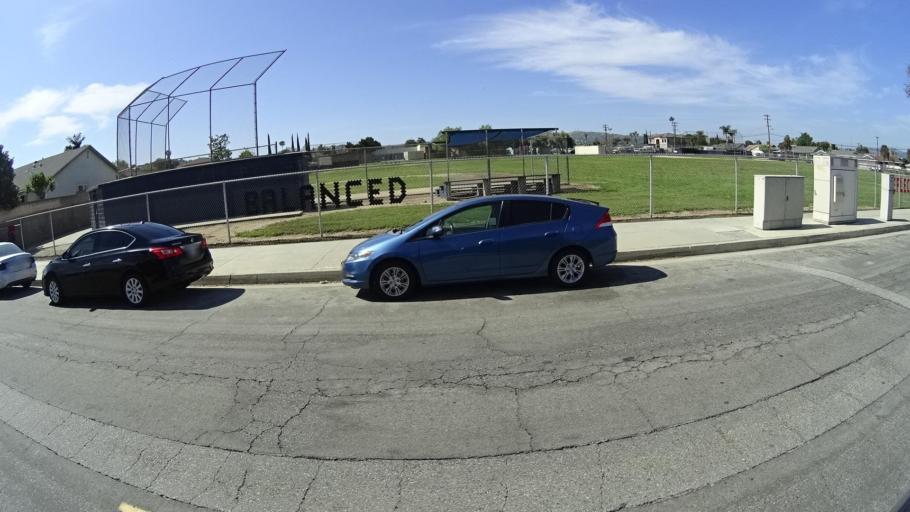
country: US
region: California
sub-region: Los Angeles County
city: Walnut
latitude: 33.9931
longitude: -117.8716
